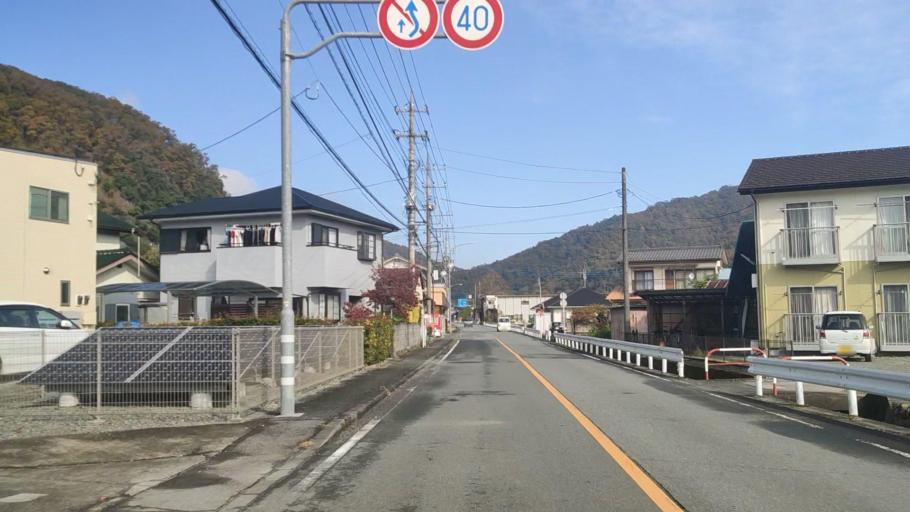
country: JP
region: Yamanashi
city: Ryuo
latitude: 35.4905
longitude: 138.4497
